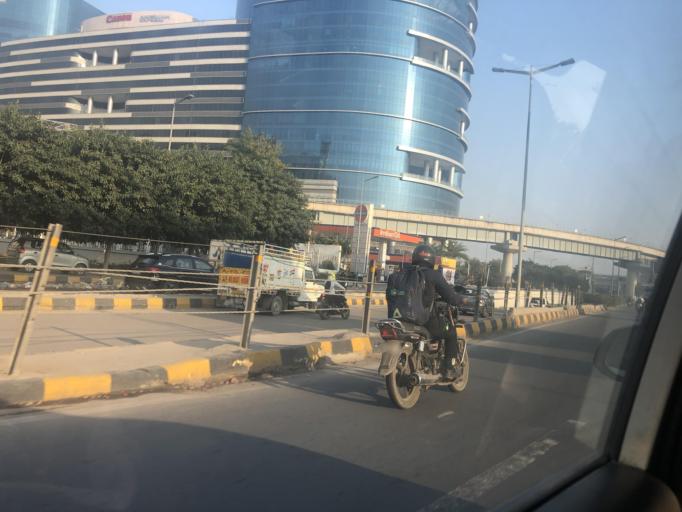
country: IN
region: Haryana
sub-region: Gurgaon
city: Gurgaon
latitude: 28.4894
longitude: 77.0902
